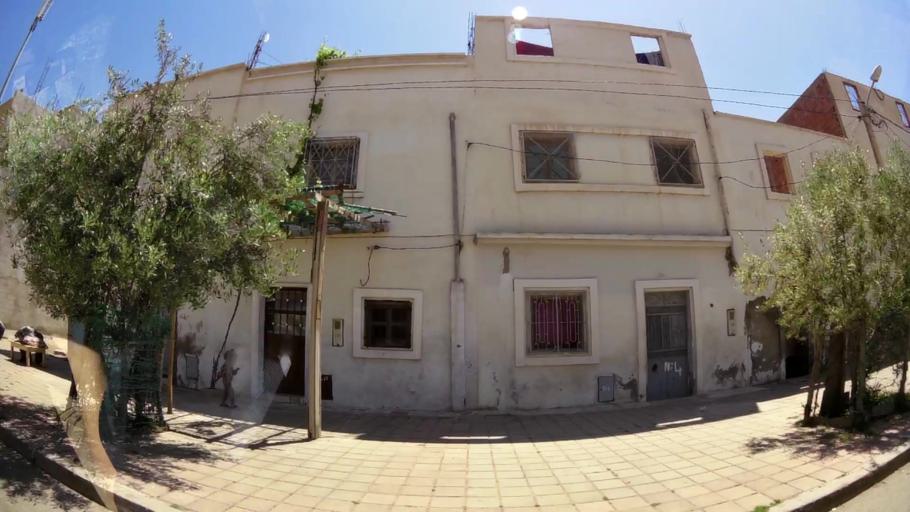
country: MA
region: Oriental
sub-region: Oujda-Angad
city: Oujda
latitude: 34.6939
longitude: -1.9430
